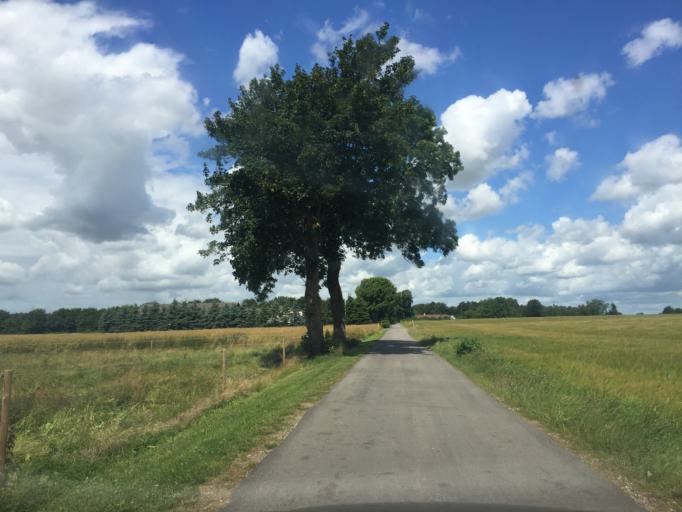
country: DK
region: Capital Region
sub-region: Hoje-Taastrup Kommune
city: Taastrup
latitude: 55.6997
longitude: 12.2700
